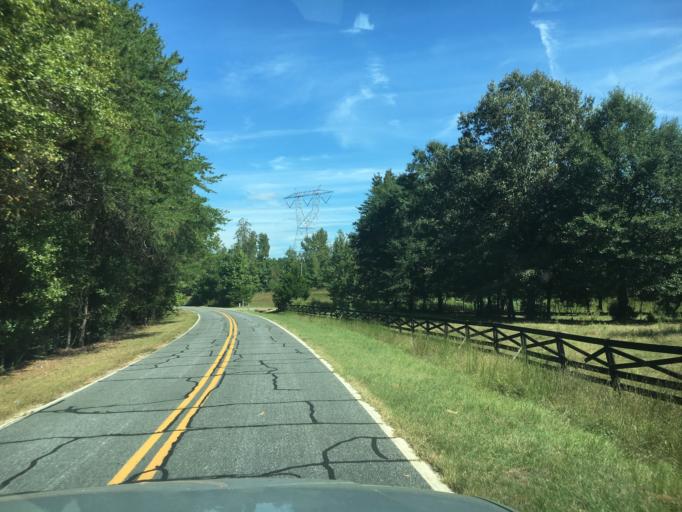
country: US
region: South Carolina
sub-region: Spartanburg County
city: Mayo
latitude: 35.1956
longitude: -81.9208
